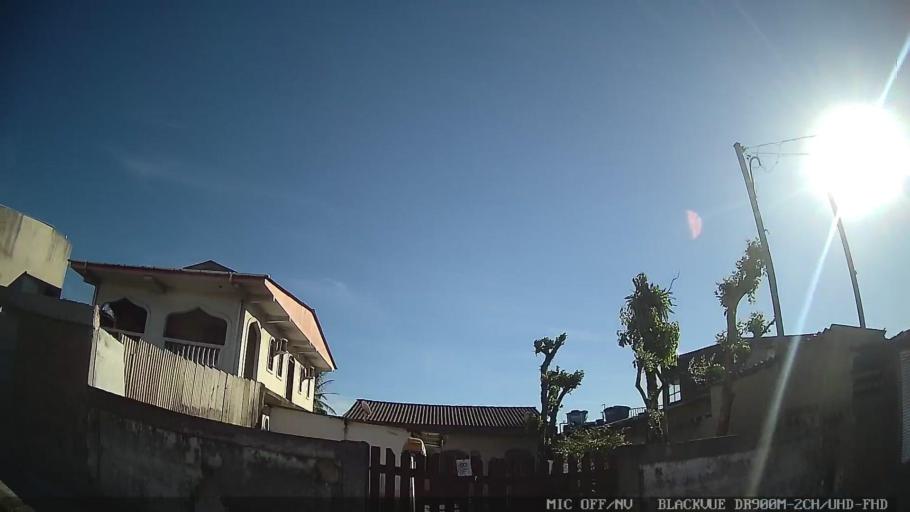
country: BR
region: Sao Paulo
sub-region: Guaruja
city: Guaruja
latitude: -23.9518
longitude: -46.2786
